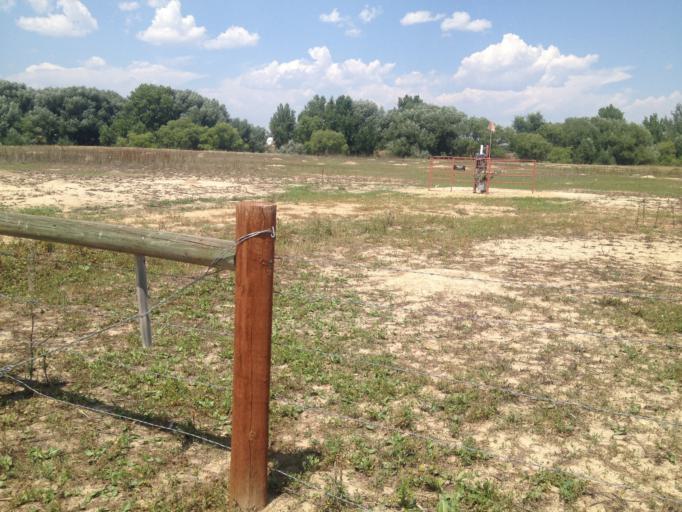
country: US
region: Colorado
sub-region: Boulder County
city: Lafayette
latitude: 39.9837
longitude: -105.0675
